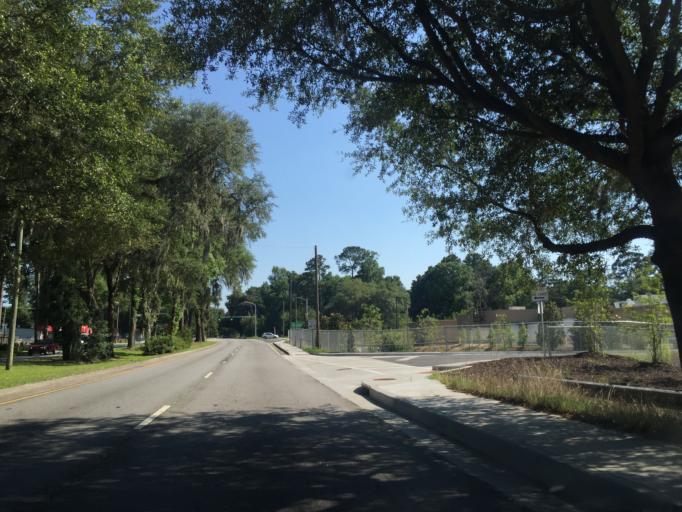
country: US
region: Georgia
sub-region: Chatham County
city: Montgomery
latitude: 31.9843
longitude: -81.1299
